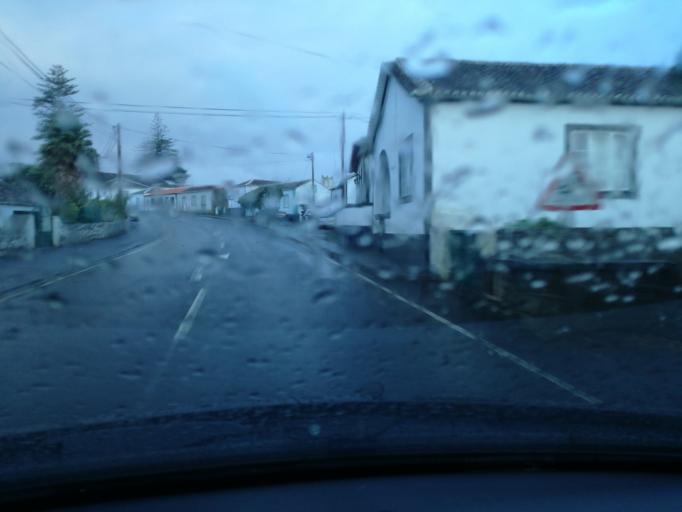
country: PT
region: Azores
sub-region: Praia da Vitoria
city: Praia da Vitoria
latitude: 38.7079
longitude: -27.0598
